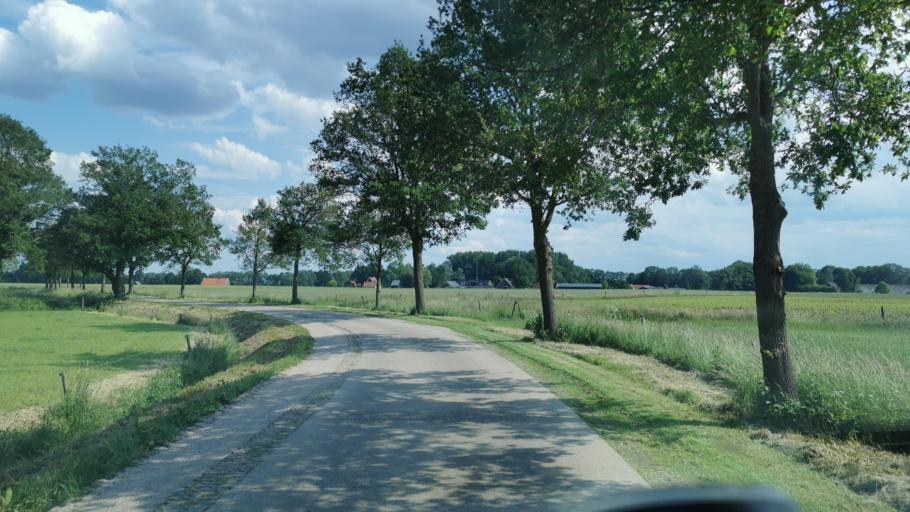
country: NL
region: Overijssel
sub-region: Gemeente Tubbergen
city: Tubbergen
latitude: 52.3456
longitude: 6.7993
